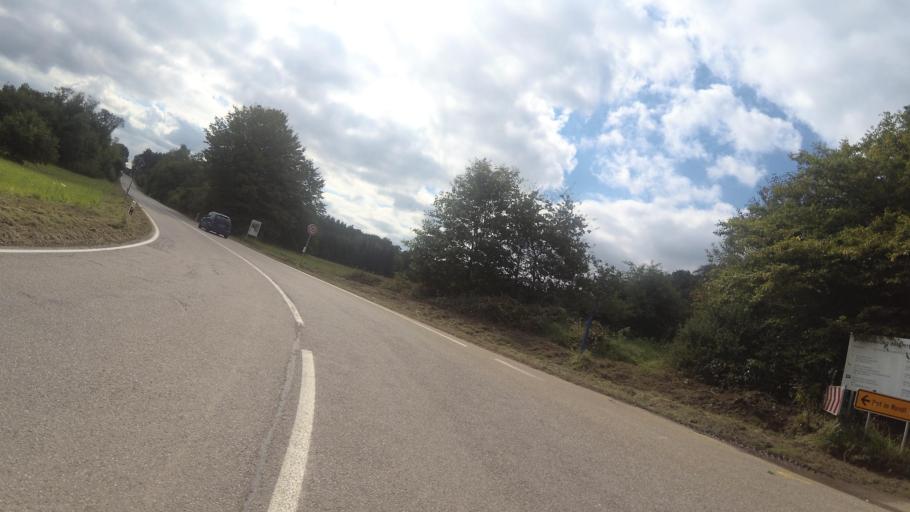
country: DE
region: Saarland
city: Grossrosseln
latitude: 49.2048
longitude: 6.8095
